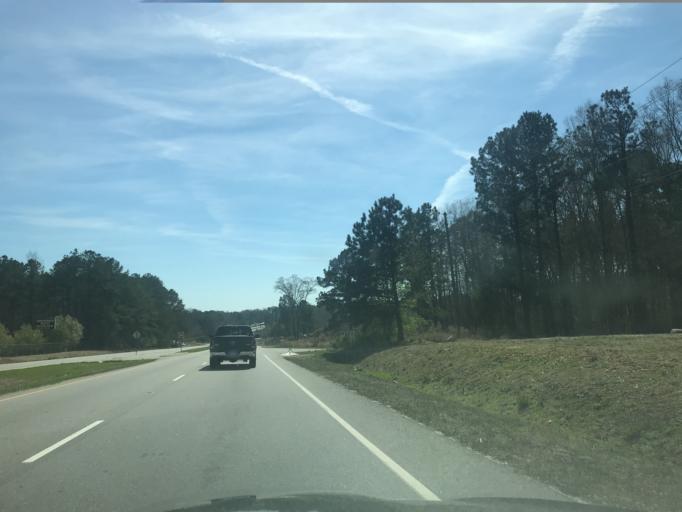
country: US
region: North Carolina
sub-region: Wake County
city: Fuquay-Varina
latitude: 35.6382
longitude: -78.7135
